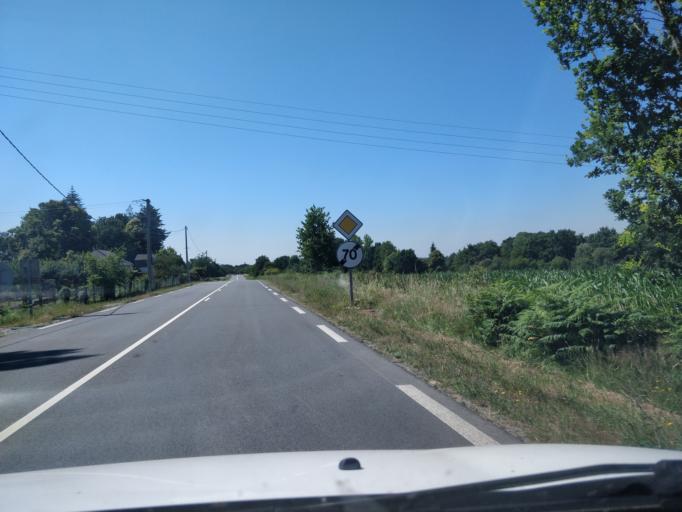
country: FR
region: Brittany
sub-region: Departement d'Ille-et-Vilaine
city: Bonnemain
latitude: 48.4613
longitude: -1.7427
